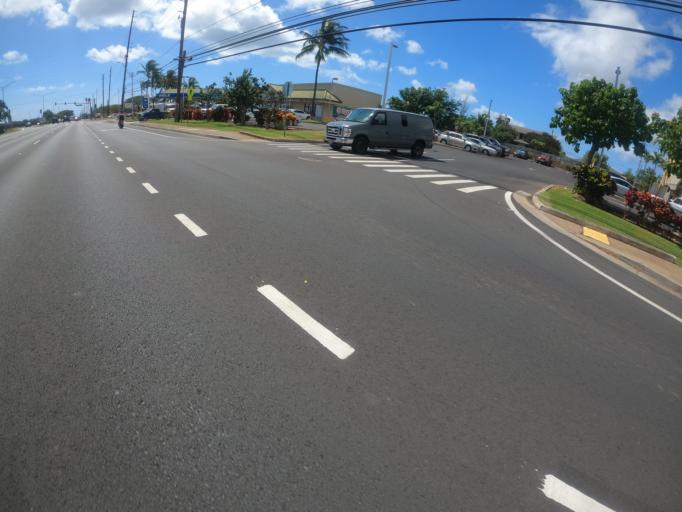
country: US
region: Hawaii
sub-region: Honolulu County
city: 'Ewa Gentry
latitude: 21.3488
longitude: -158.0273
